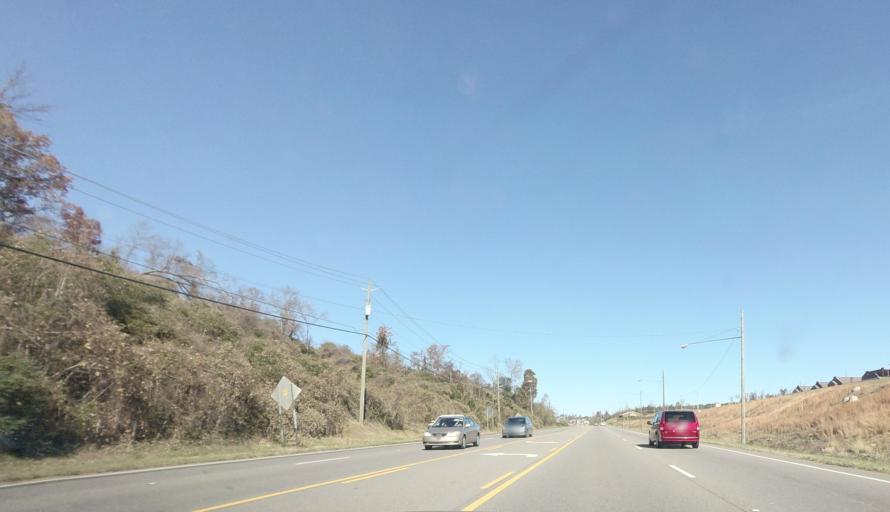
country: US
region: Alabama
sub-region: Jefferson County
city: Fultondale
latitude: 33.5947
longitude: -86.8016
